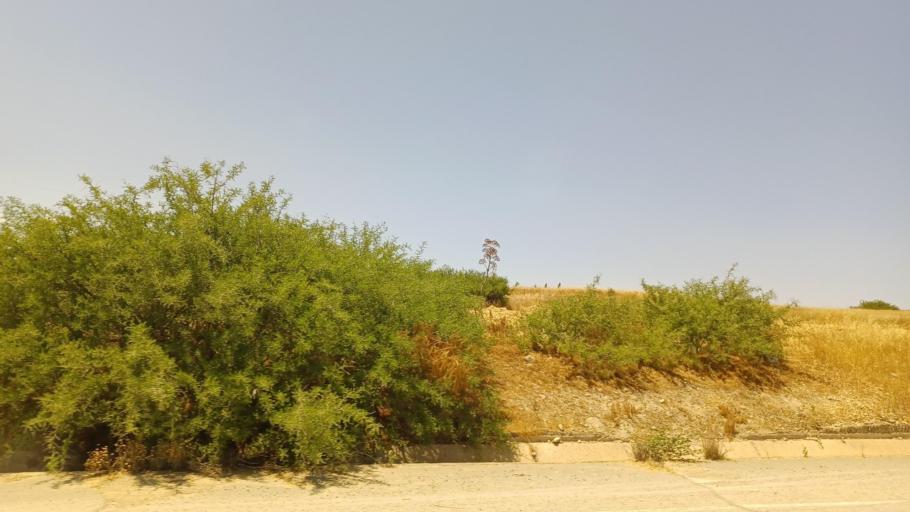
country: CY
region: Larnaka
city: Pyla
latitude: 35.0031
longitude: 33.7036
